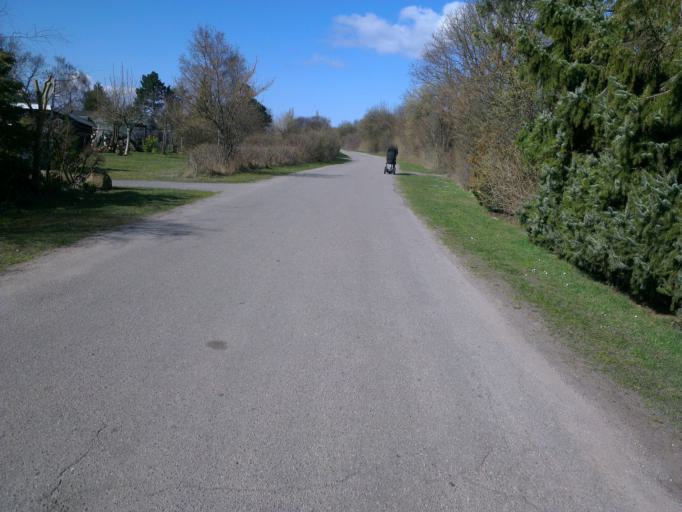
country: DK
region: Capital Region
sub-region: Halsnaes Kommune
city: Hundested
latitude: 55.9343
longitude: 11.9169
